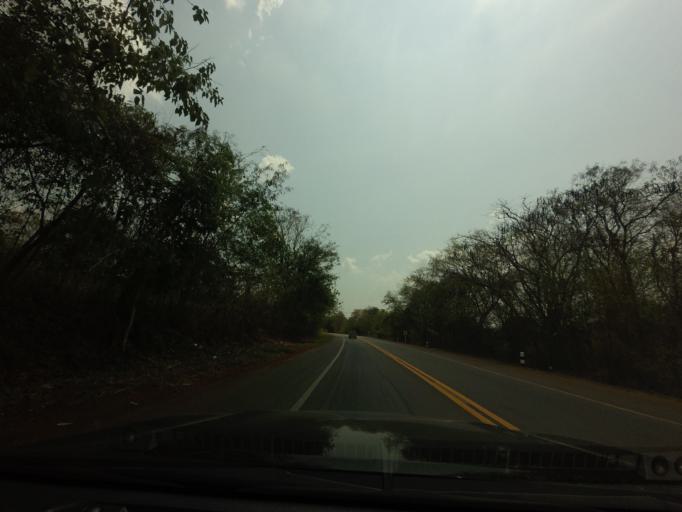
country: TH
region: Kanchanaburi
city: Sai Yok
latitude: 14.1393
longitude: 99.1488
